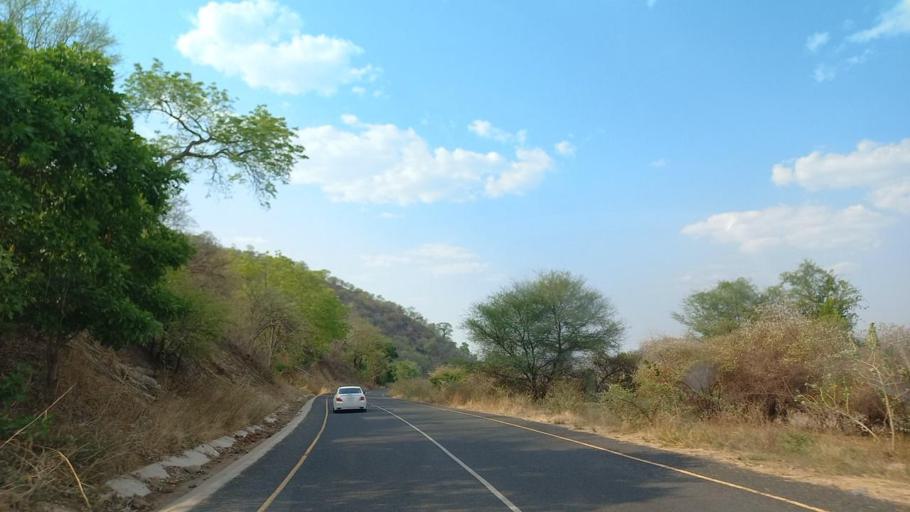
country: ZM
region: Lusaka
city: Luangwa
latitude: -15.0082
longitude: 30.2157
